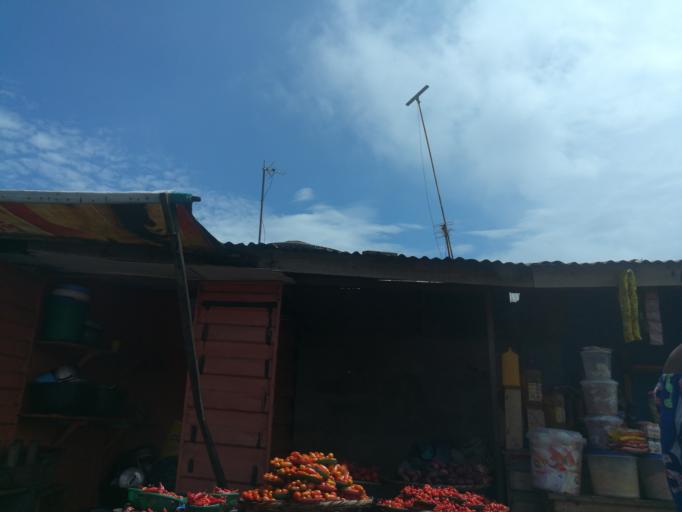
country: NG
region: Lagos
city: Agege
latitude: 6.6231
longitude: 3.3314
